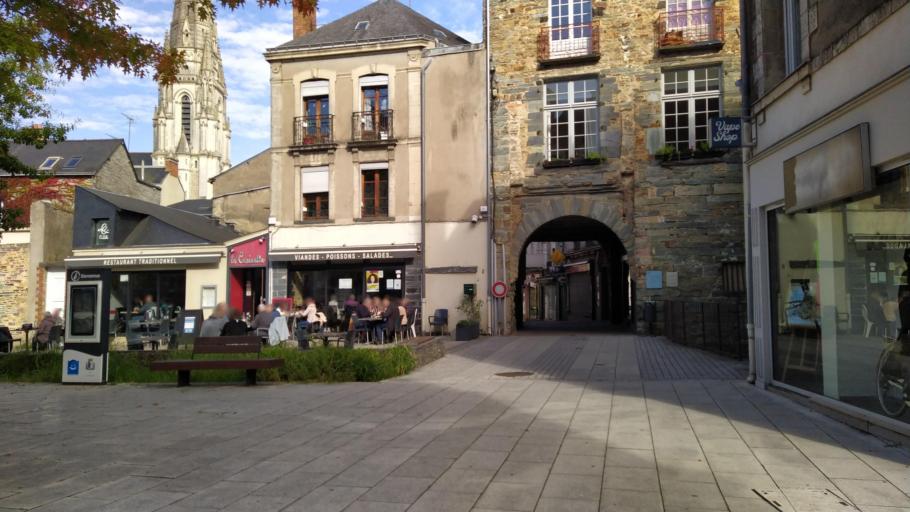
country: FR
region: Pays de la Loire
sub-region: Departement de la Loire-Atlantique
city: Chateaubriant
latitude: 47.7180
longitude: -1.3768
